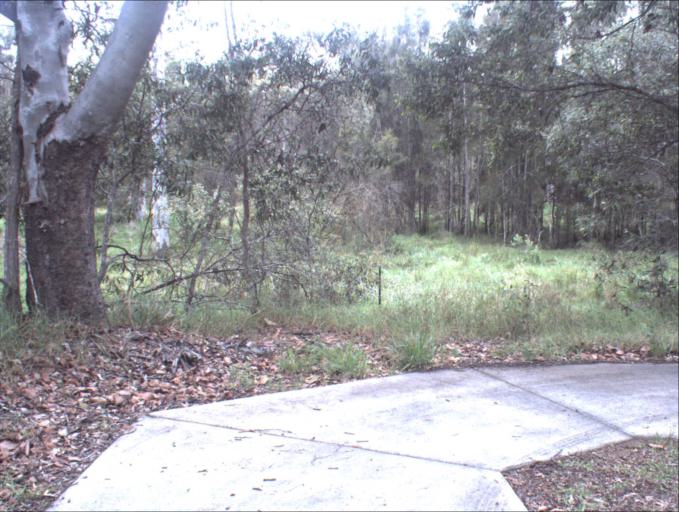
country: AU
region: Queensland
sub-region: Logan
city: Logan Reserve
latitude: -27.6788
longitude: 153.0683
